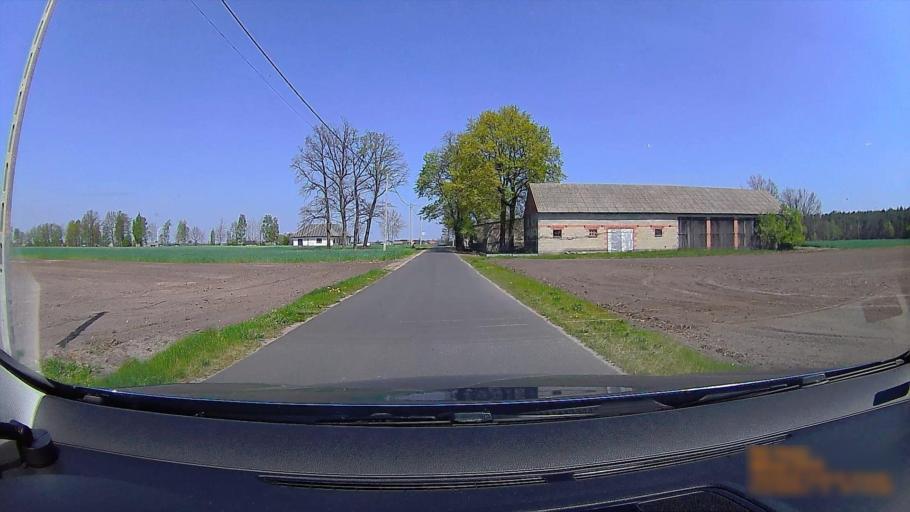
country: PL
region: Greater Poland Voivodeship
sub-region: Powiat koninski
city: Rychwal
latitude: 52.1000
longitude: 18.1846
